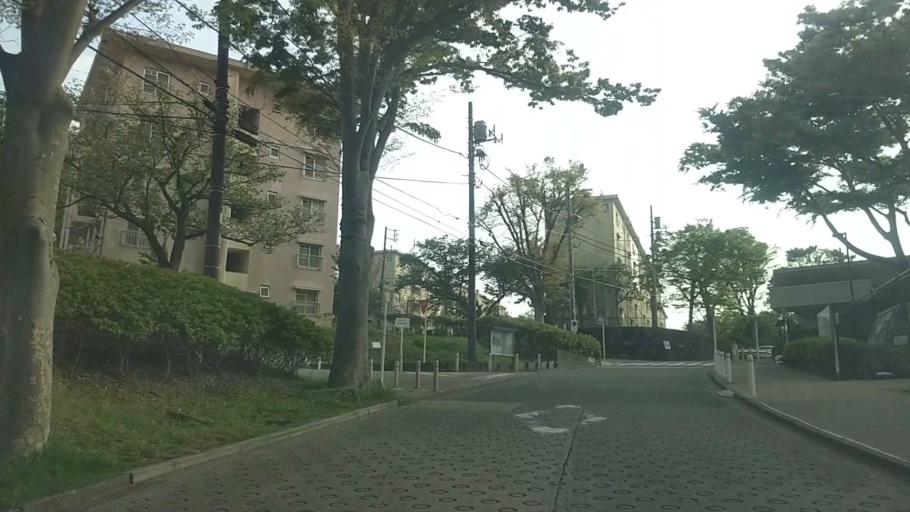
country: JP
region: Kanagawa
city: Kamakura
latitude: 35.3595
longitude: 139.5577
